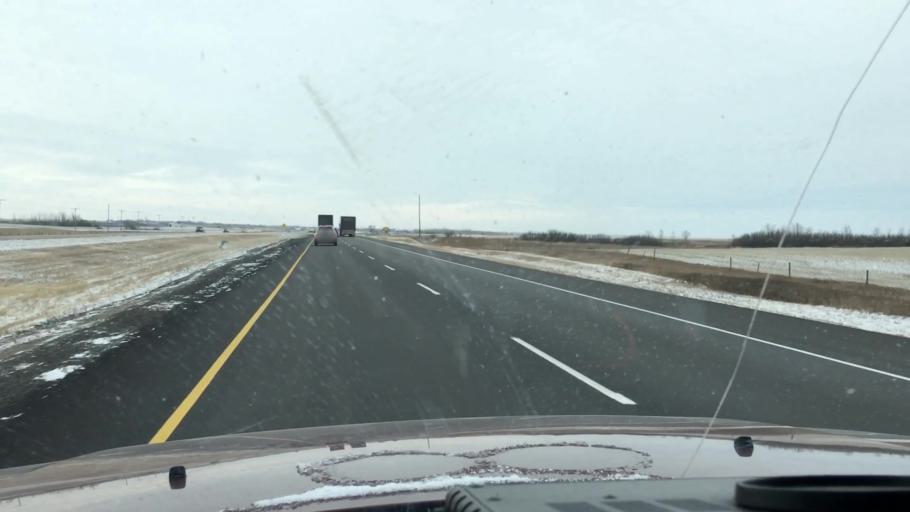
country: CA
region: Saskatchewan
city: Saskatoon
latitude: 51.7863
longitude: -106.4808
